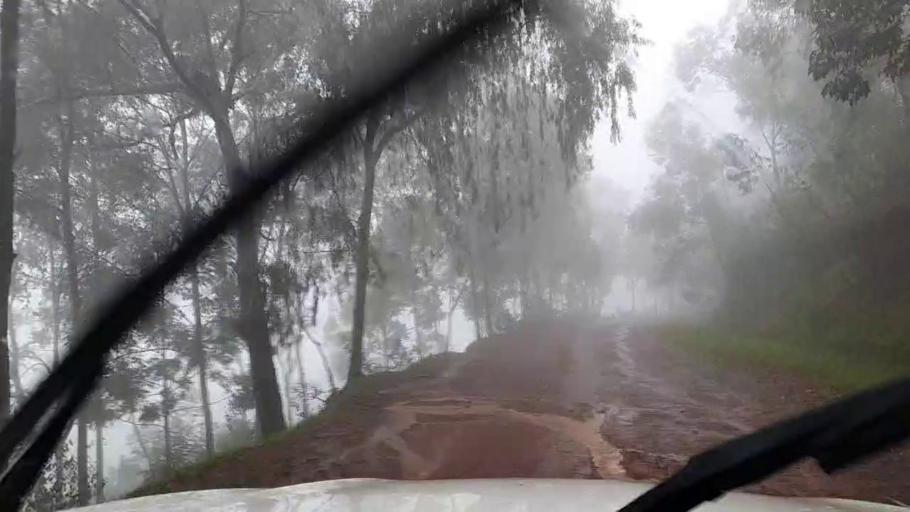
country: RW
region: Kigali
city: Kigali
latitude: -1.7685
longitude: 29.9952
